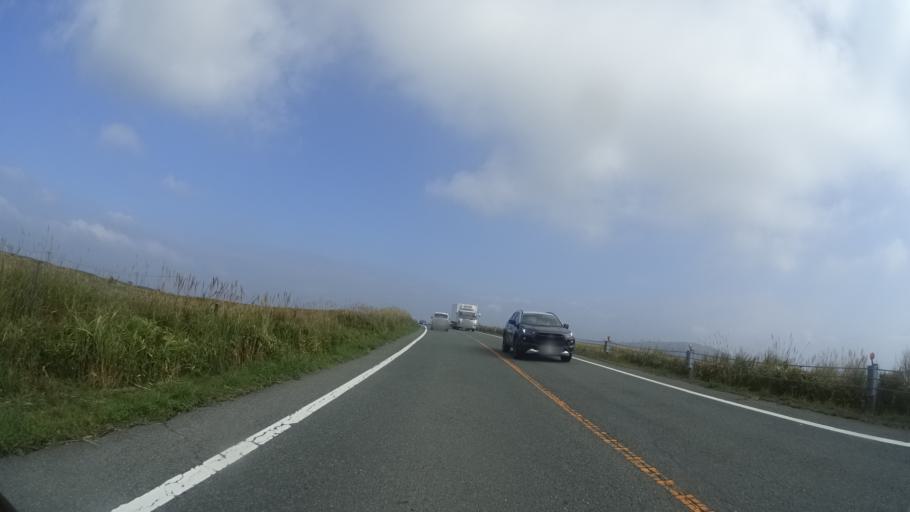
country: JP
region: Kumamoto
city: Aso
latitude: 33.0105
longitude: 131.0384
